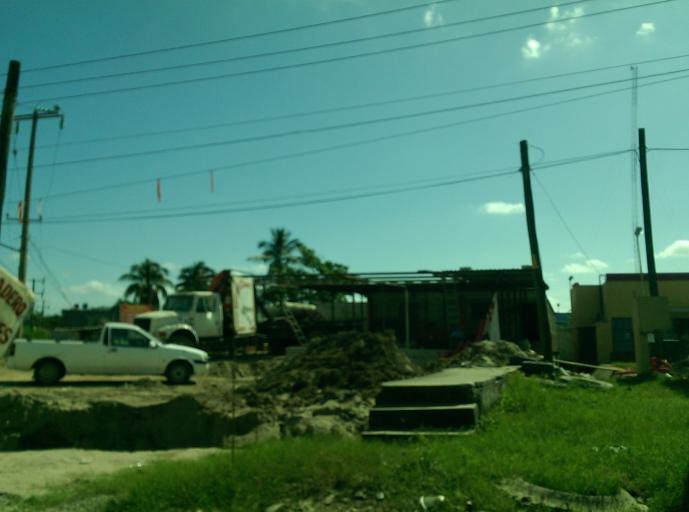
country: MX
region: Tabasco
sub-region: Centro
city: Anacleto Canabal 2da. Seccion
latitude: 17.9834
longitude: -93.0119
